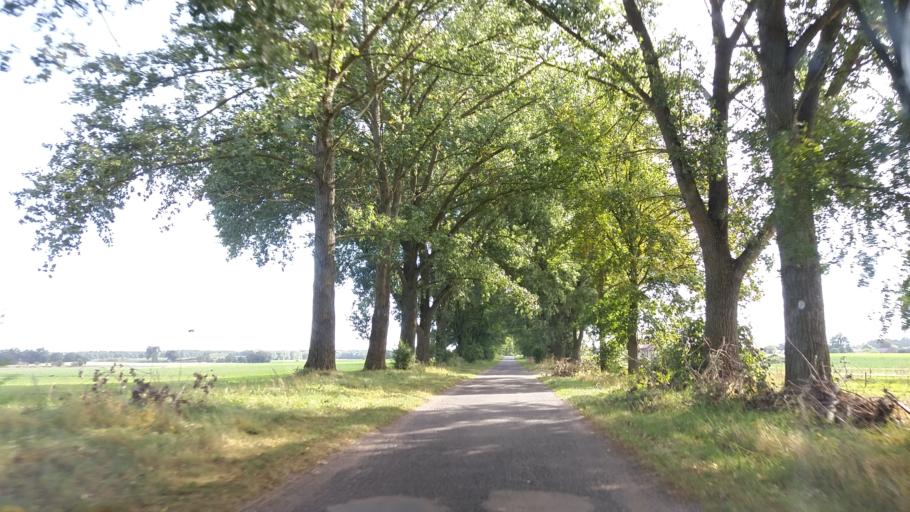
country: PL
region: West Pomeranian Voivodeship
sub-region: Powiat stargardzki
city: Suchan
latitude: 53.2291
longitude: 15.3686
